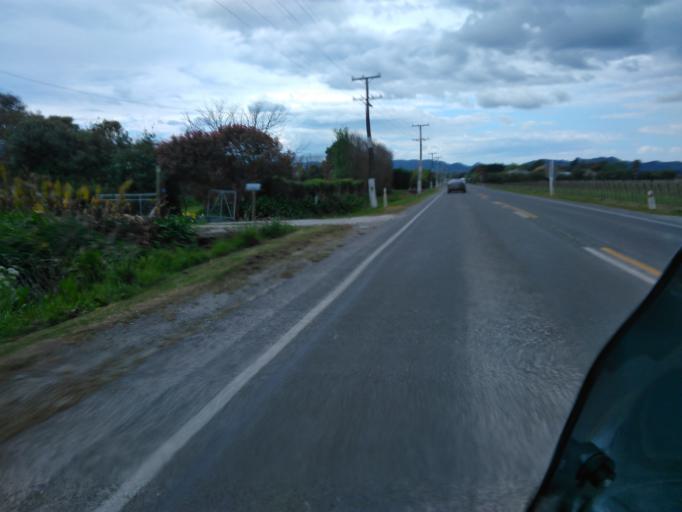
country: NZ
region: Gisborne
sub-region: Gisborne District
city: Gisborne
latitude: -38.6539
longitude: 177.9552
